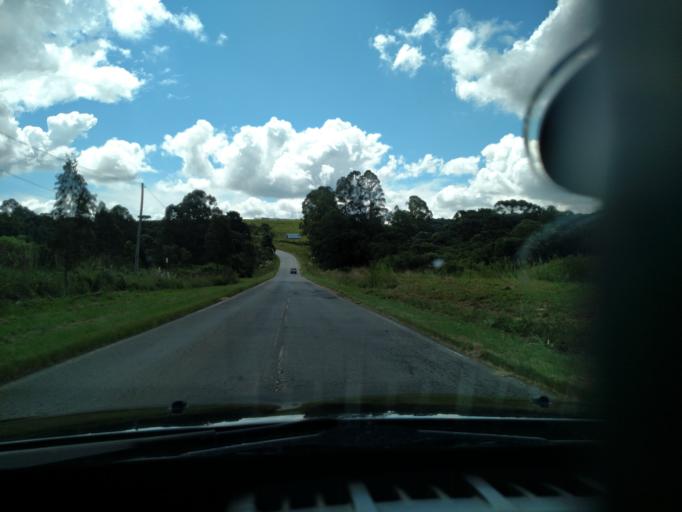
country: BR
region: Santa Catarina
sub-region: Lages
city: Lages
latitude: -27.8203
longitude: -50.2554
